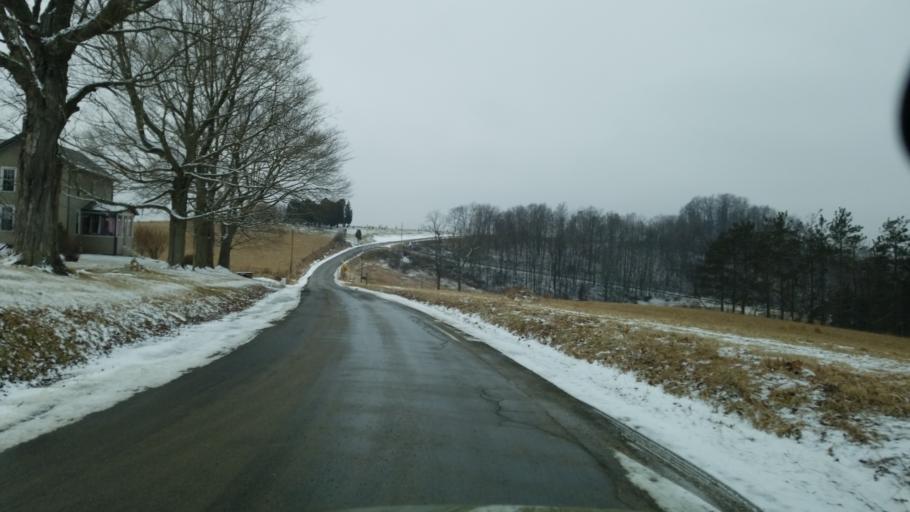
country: US
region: Pennsylvania
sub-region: Jefferson County
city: Sykesville
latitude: 41.0851
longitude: -78.8342
